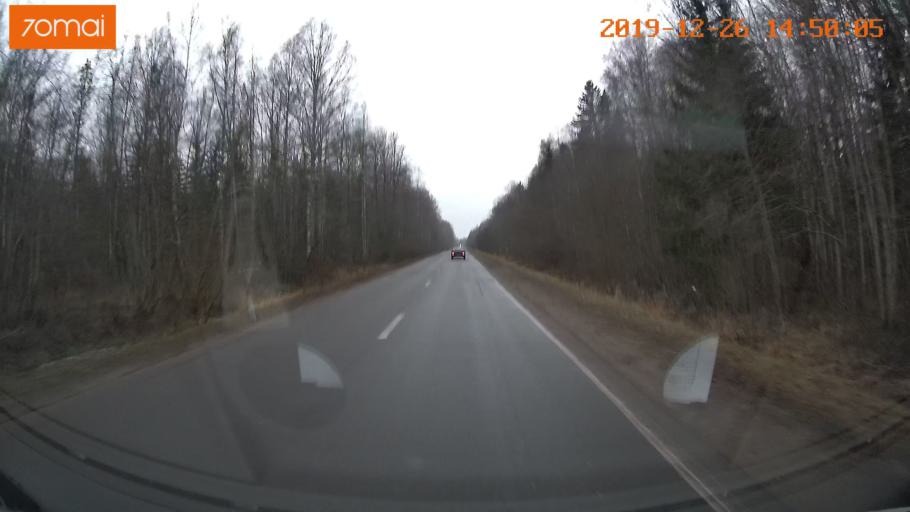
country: RU
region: Jaroslavl
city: Poshekhon'ye
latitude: 58.3348
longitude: 38.9323
